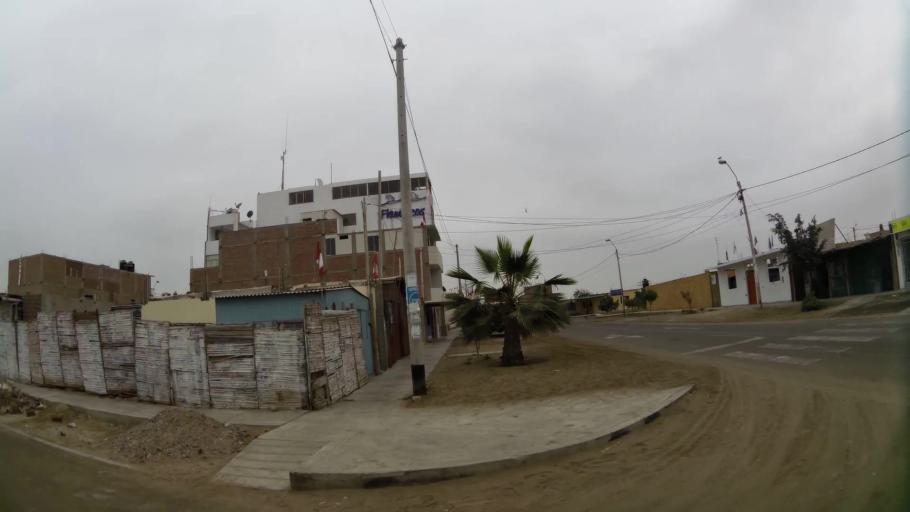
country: PE
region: Ica
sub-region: Provincia de Pisco
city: Paracas
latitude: -13.8375
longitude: -76.2481
